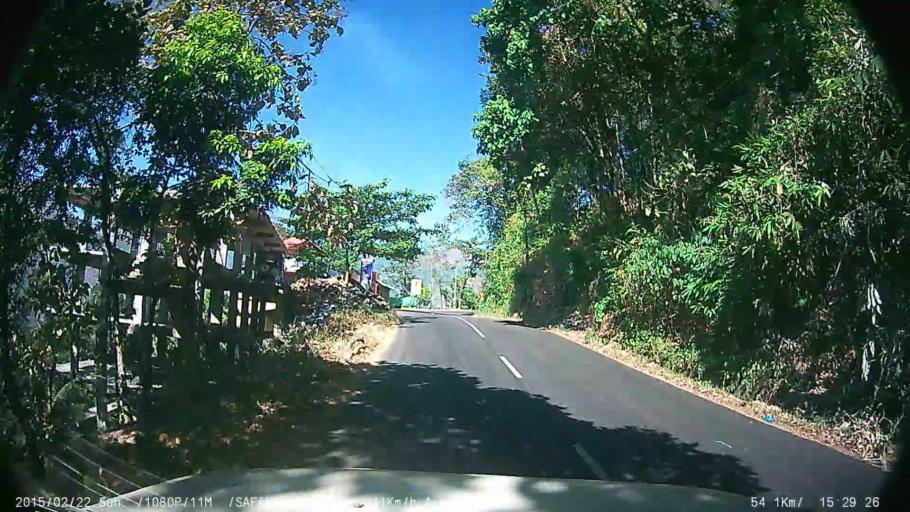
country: IN
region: Kerala
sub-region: Kottayam
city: Erattupetta
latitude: 9.5579
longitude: 76.9475
